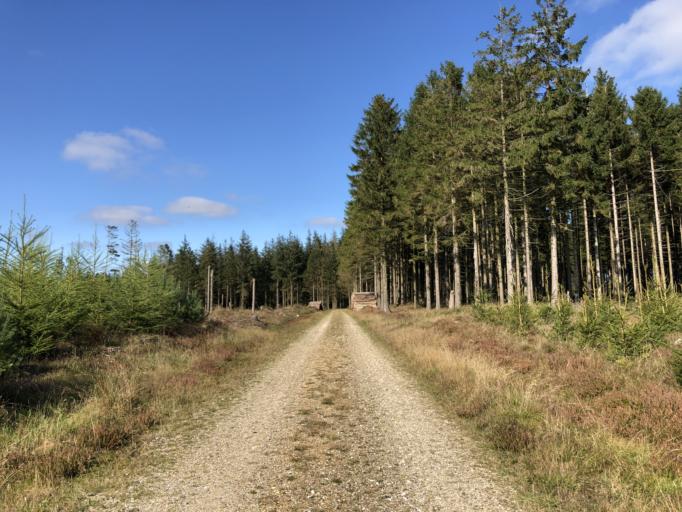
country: DK
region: Central Jutland
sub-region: Holstebro Kommune
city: Holstebro
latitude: 56.2474
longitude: 8.5012
